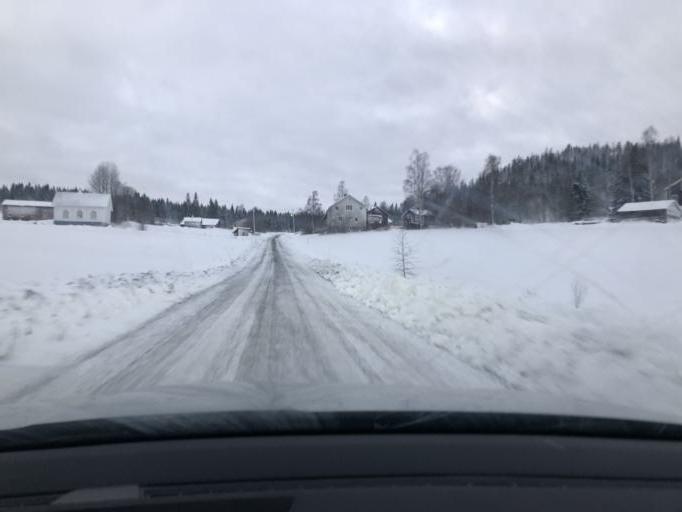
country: SE
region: Vaesternorrland
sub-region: Kramfors Kommun
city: Nordingra
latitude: 62.9130
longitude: 18.2343
